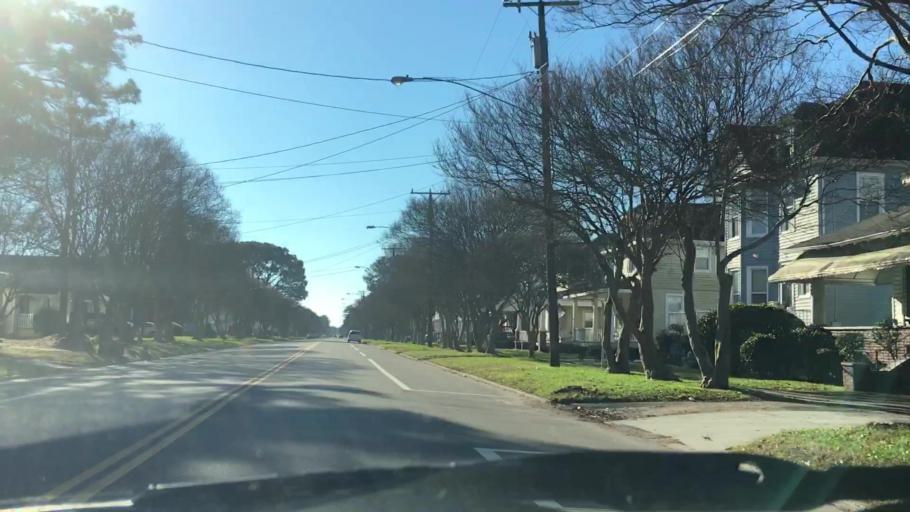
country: US
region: Virginia
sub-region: City of Norfolk
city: Norfolk
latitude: 36.8728
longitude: -76.2529
